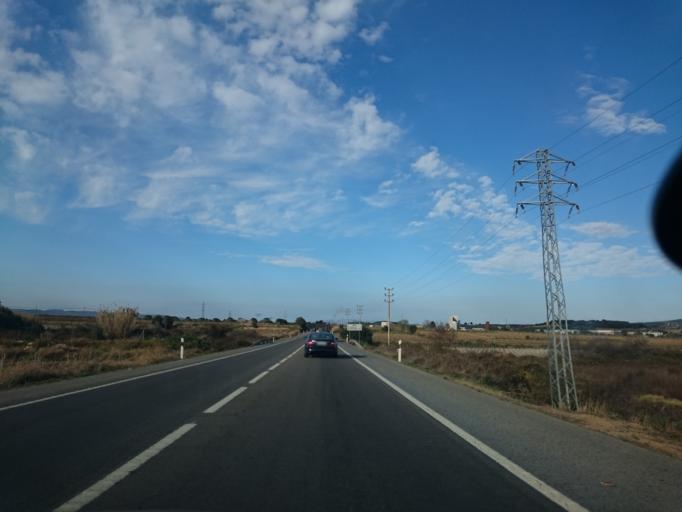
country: ES
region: Catalonia
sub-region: Provincia de Barcelona
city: Castellet
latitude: 41.2715
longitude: 1.6088
